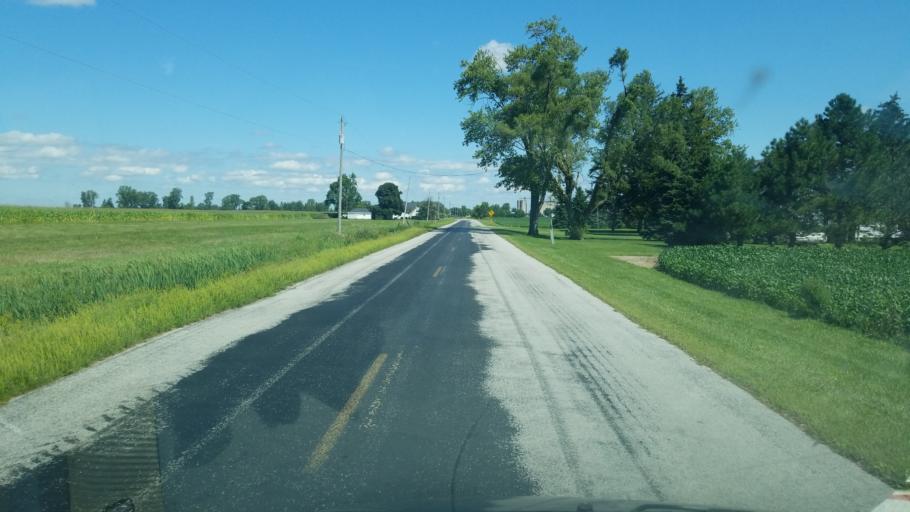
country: US
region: Ohio
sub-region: Henry County
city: Deshler
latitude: 41.2703
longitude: -83.8438
